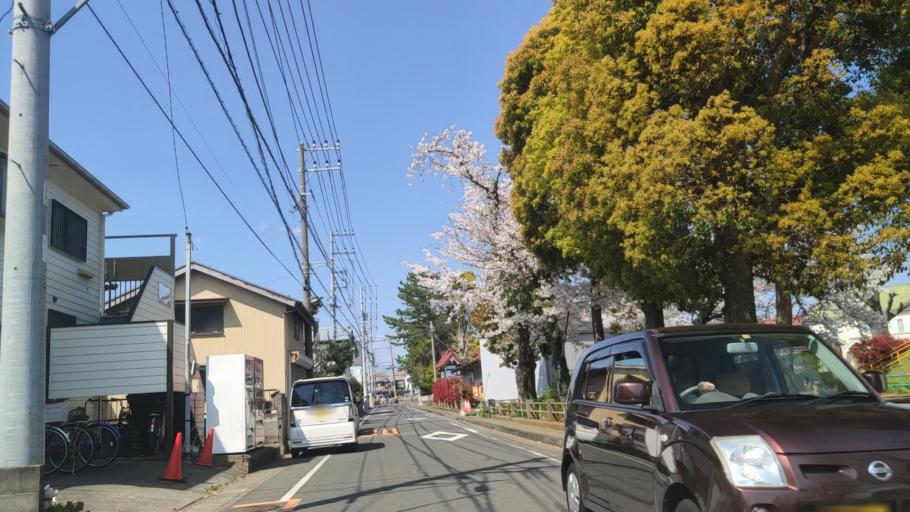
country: JP
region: Kanagawa
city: Hiratsuka
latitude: 35.3356
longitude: 139.3311
